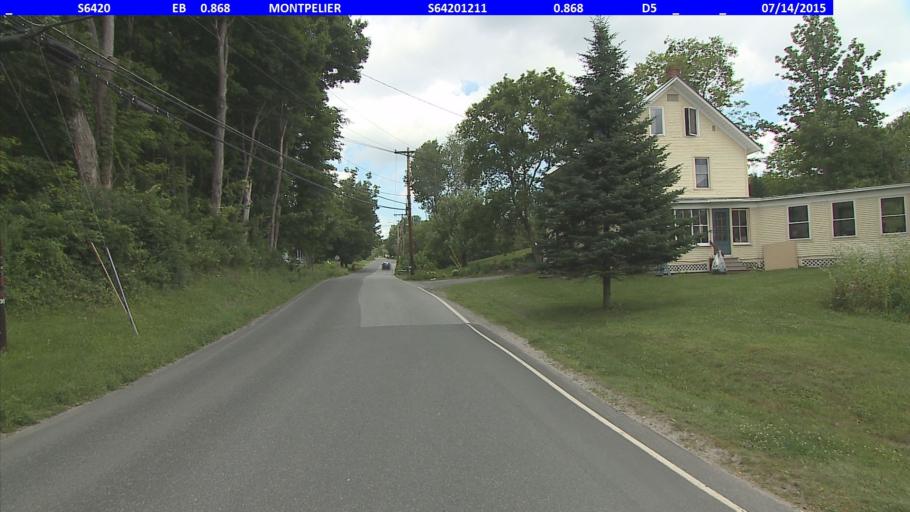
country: US
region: Vermont
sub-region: Washington County
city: Montpelier
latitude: 44.2621
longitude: -72.5583
